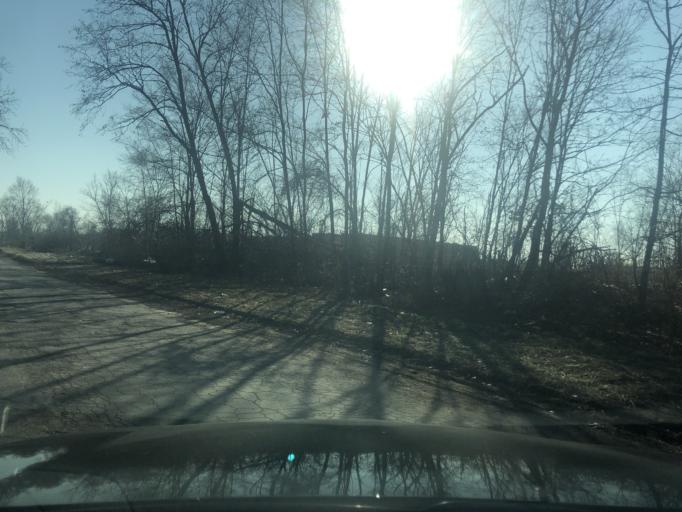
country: US
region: Michigan
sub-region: Wayne County
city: River Rouge
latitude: 42.3080
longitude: -83.0971
